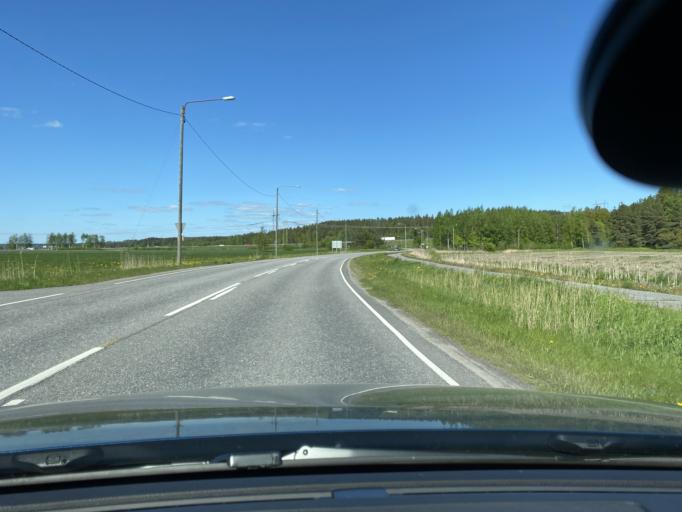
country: FI
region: Varsinais-Suomi
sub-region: Turku
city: Paimio
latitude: 60.4215
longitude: 22.6645
